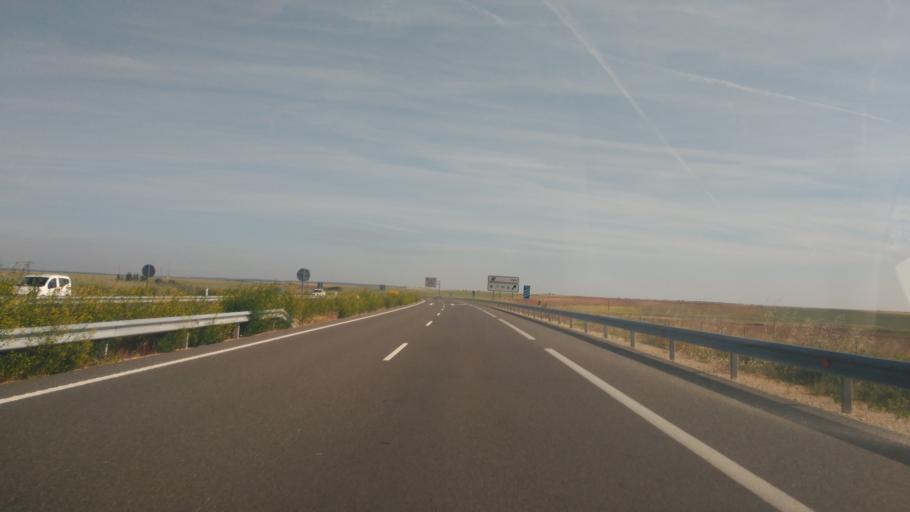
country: ES
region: Castille and Leon
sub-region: Provincia de Salamanca
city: Calzada de Valdunciel
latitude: 41.0796
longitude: -5.6876
